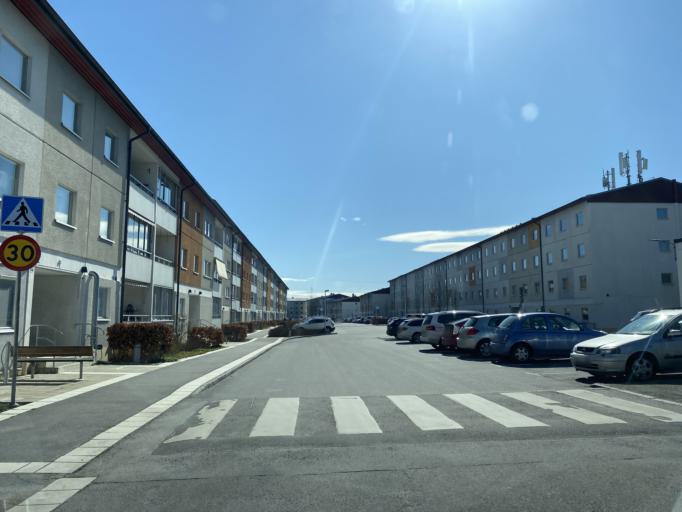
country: SE
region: Stockholm
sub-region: Stockholms Kommun
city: Arsta
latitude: 59.2849
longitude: 18.0374
